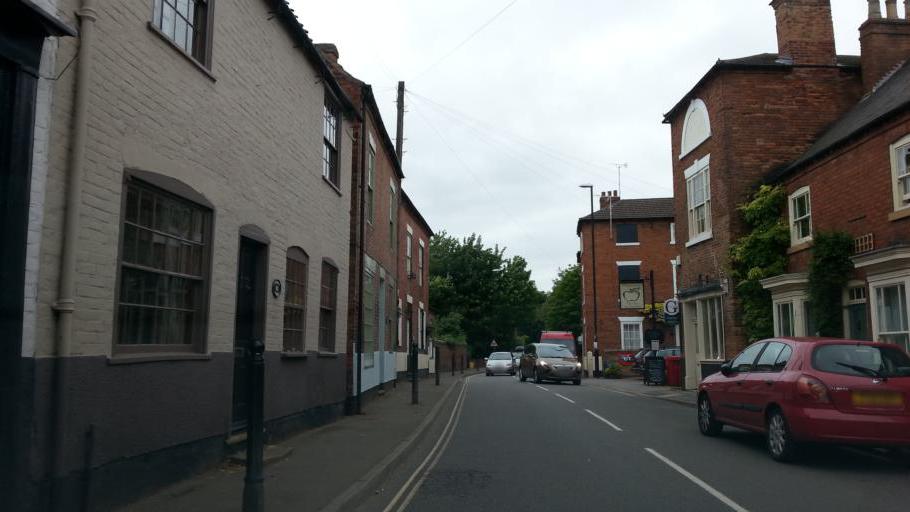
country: GB
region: England
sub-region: Nottinghamshire
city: Southwell
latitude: 53.0762
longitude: -0.9485
